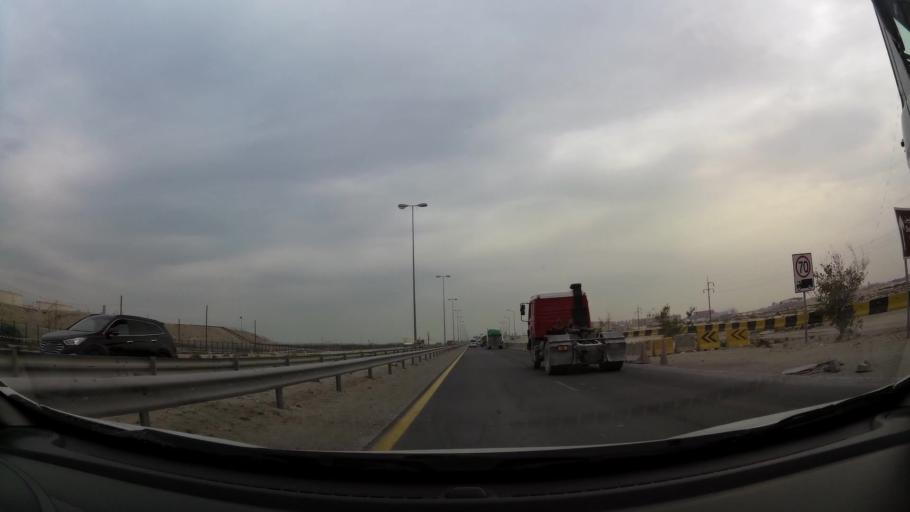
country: BH
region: Northern
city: Ar Rifa'
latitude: 26.1101
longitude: 50.5980
